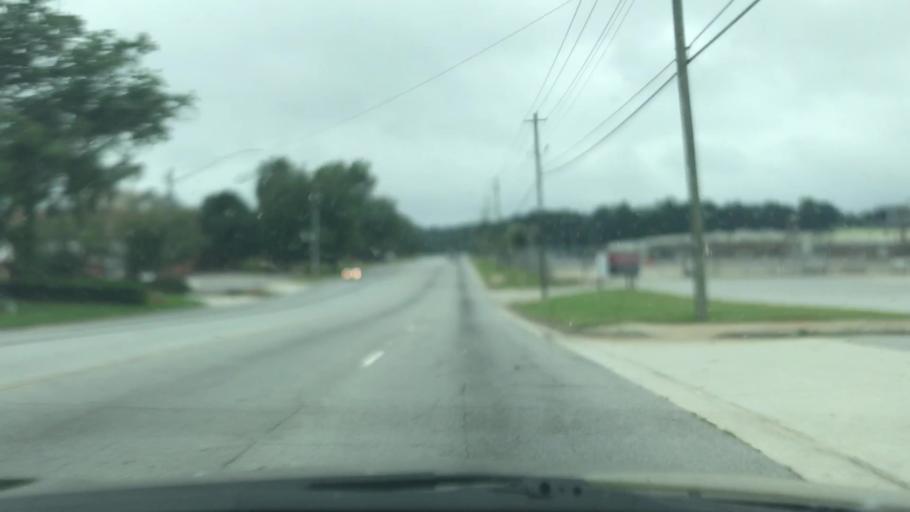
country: US
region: Georgia
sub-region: DeKalb County
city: Tucker
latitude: 33.8499
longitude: -84.2008
